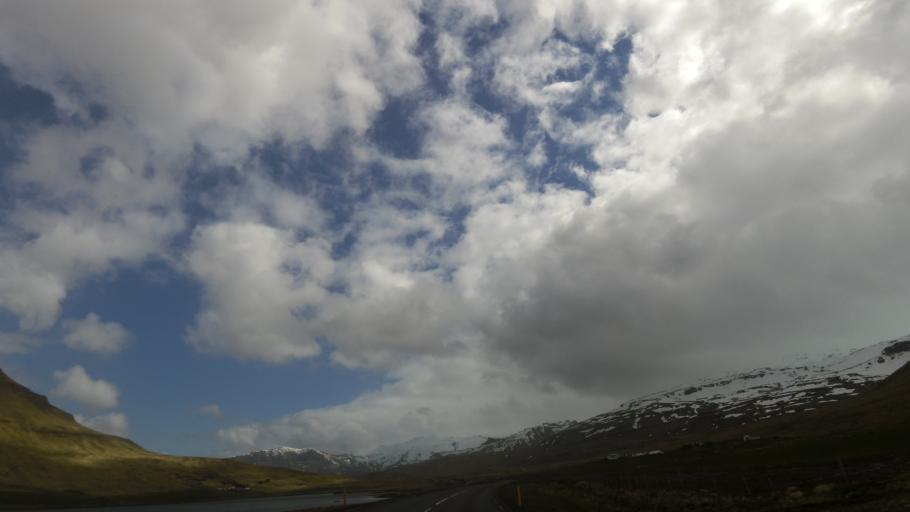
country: IS
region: West
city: Olafsvik
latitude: 64.9341
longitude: -23.3343
